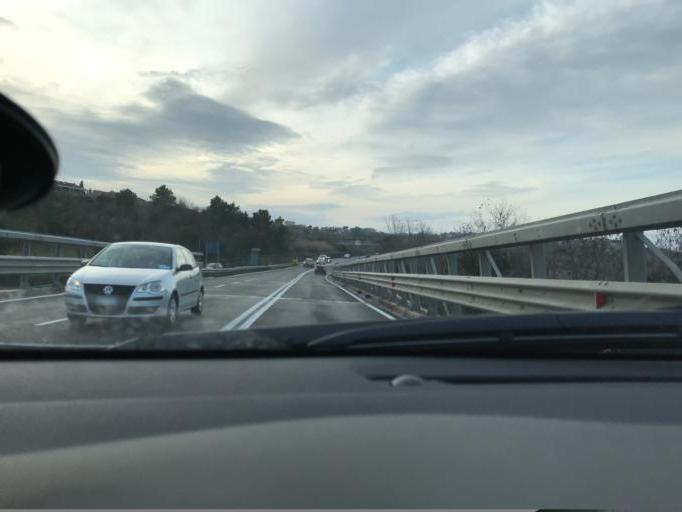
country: IT
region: The Marches
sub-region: Provincia di Ancona
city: Posatora
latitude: 43.5969
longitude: 13.4477
